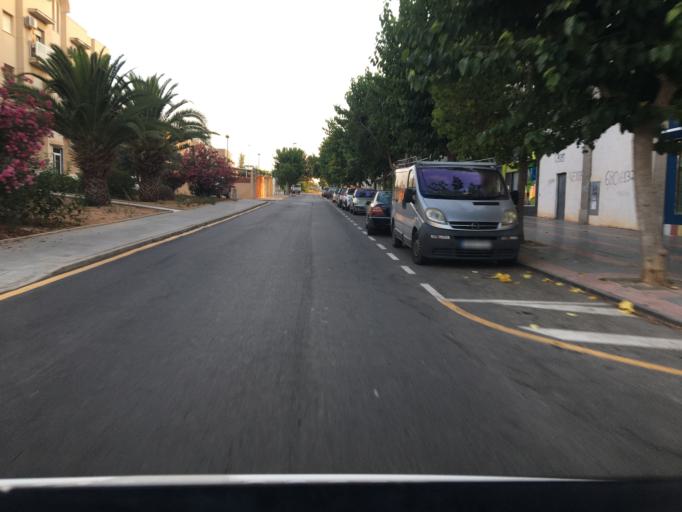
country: ES
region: Murcia
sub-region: Murcia
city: Cartagena
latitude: 37.6260
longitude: -0.9835
